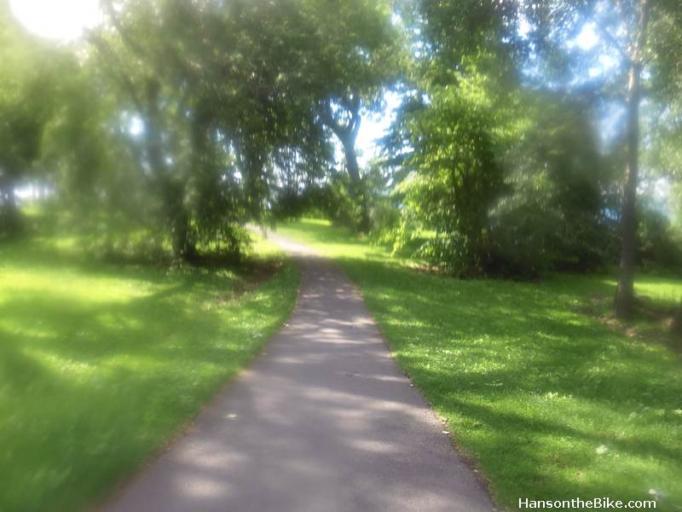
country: CA
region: Ontario
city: Kingston
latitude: 44.2148
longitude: -76.5294
